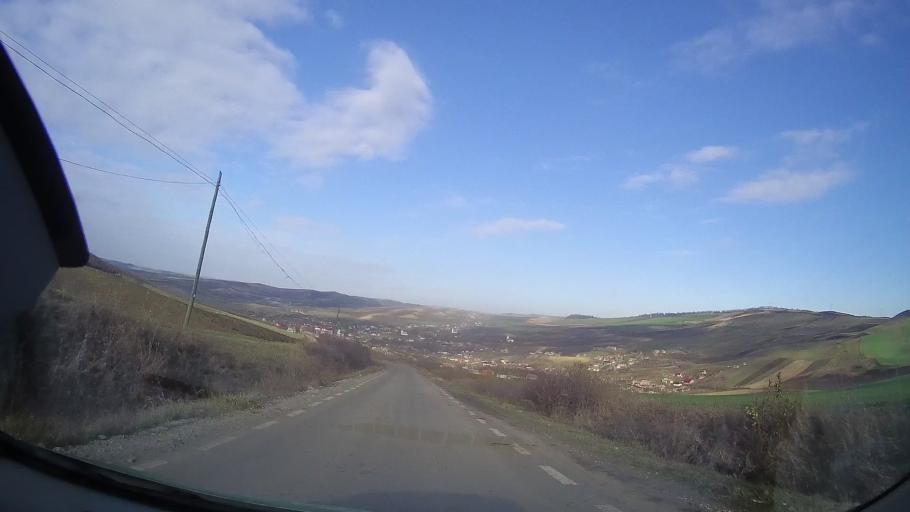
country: RO
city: Barza
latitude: 46.5462
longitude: 24.1474
